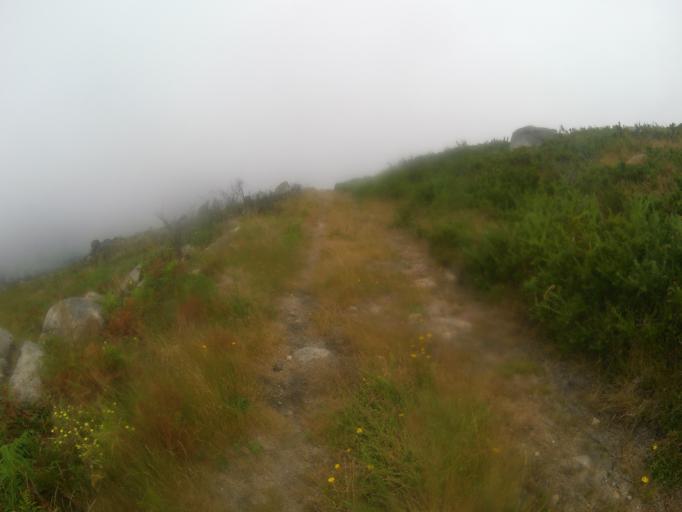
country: PT
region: Viana do Castelo
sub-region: Ponte de Lima
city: Ponte de Lima
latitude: 41.7118
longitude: -8.6007
